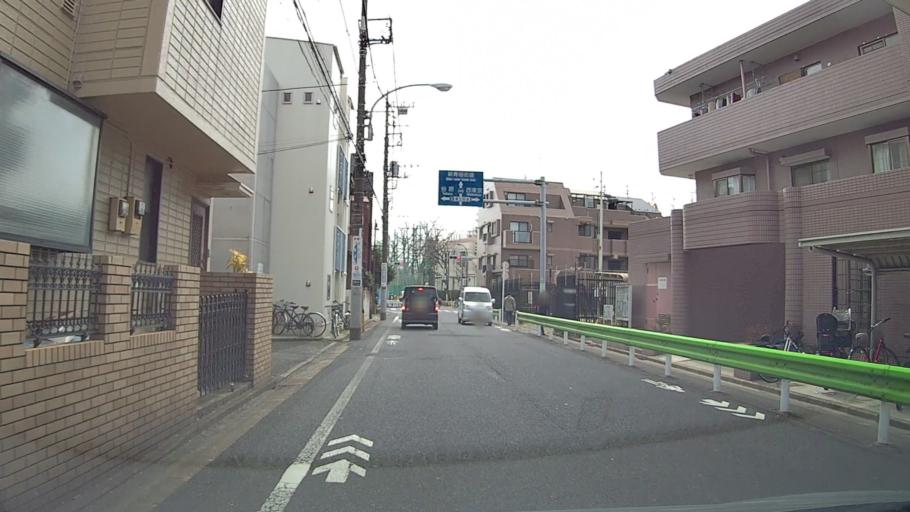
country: JP
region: Tokyo
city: Musashino
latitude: 35.7424
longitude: 139.5967
